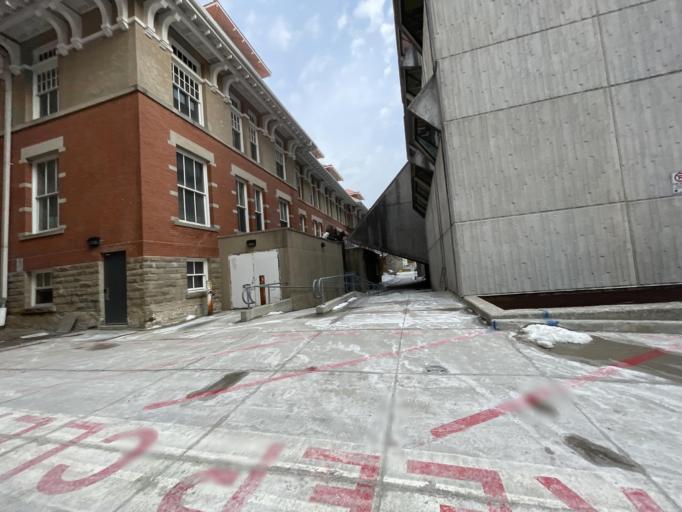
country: CA
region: Ontario
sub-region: Wellington County
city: Guelph
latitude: 43.5311
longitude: -80.2276
